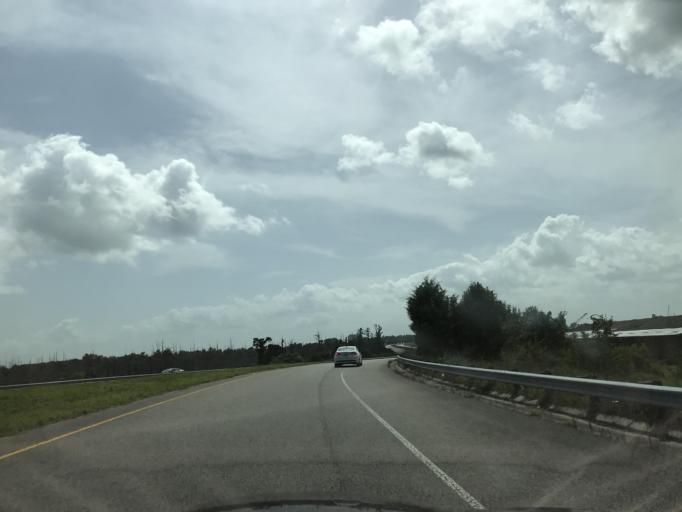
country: US
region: North Carolina
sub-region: New Hanover County
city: Wrightsboro
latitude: 34.2614
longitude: -77.9318
